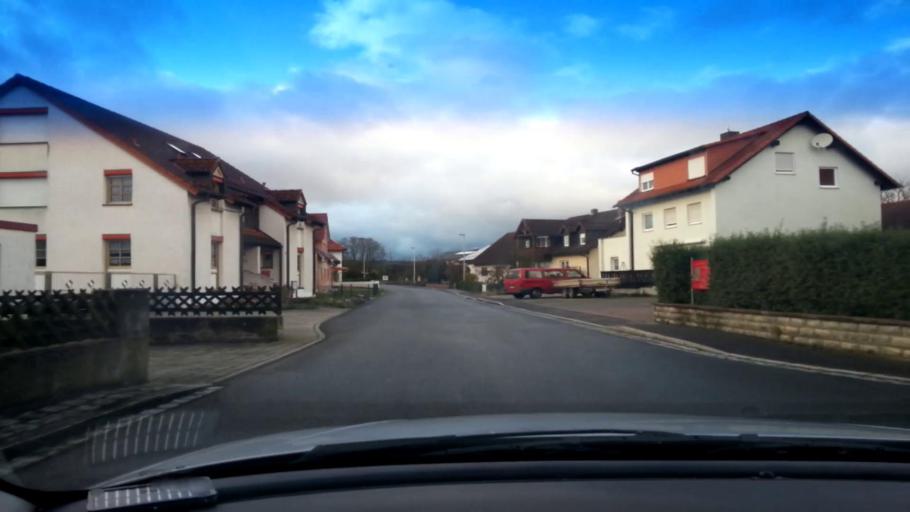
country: DE
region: Bavaria
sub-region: Upper Franconia
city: Rattelsdorf
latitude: 50.0079
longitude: 10.9021
